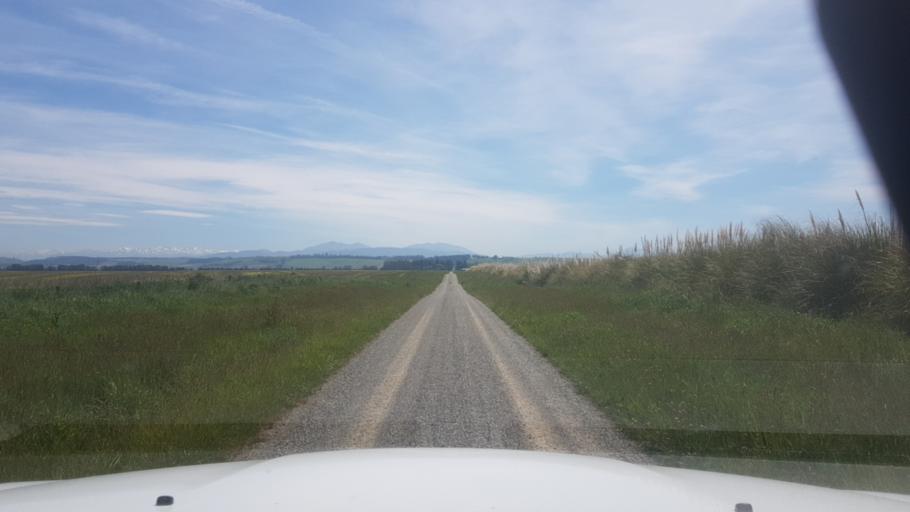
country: NZ
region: Canterbury
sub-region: Timaru District
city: Pleasant Point
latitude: -44.2355
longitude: 171.1682
